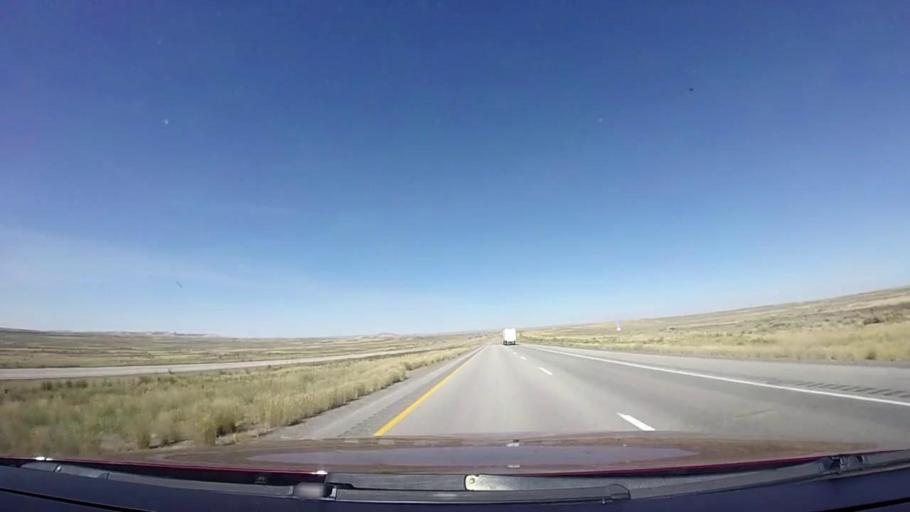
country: US
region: Wyoming
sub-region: Sweetwater County
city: Rock Springs
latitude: 41.6322
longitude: -108.3564
